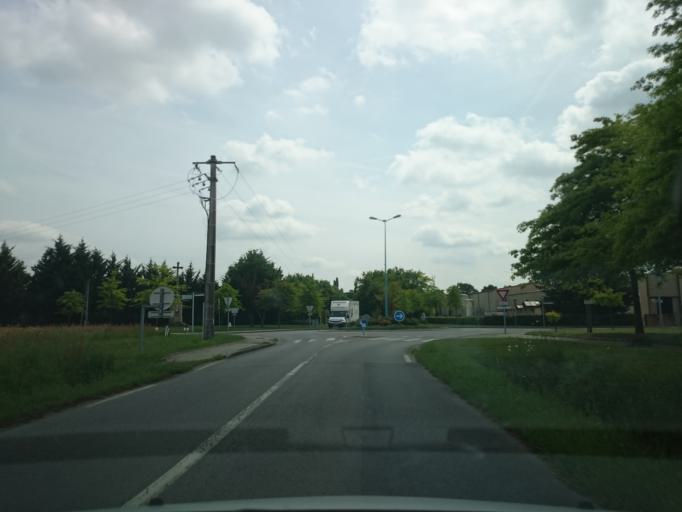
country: FR
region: Pays de la Loire
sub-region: Departement de la Loire-Atlantique
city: Pont-Saint-Martin
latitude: 47.1168
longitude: -1.5804
